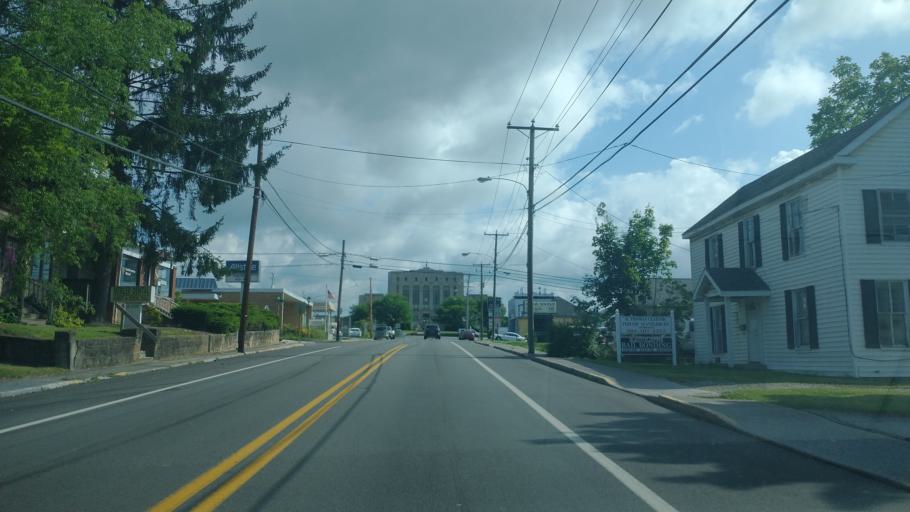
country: US
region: West Virginia
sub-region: Mercer County
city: Princeton
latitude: 37.3636
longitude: -81.1039
